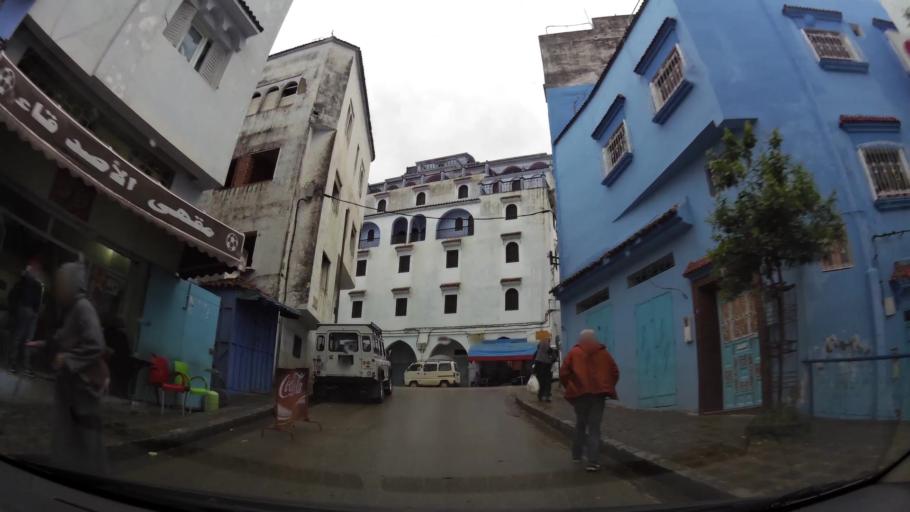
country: MA
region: Tanger-Tetouan
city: Chefchaouene
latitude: 35.1696
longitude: -5.2657
